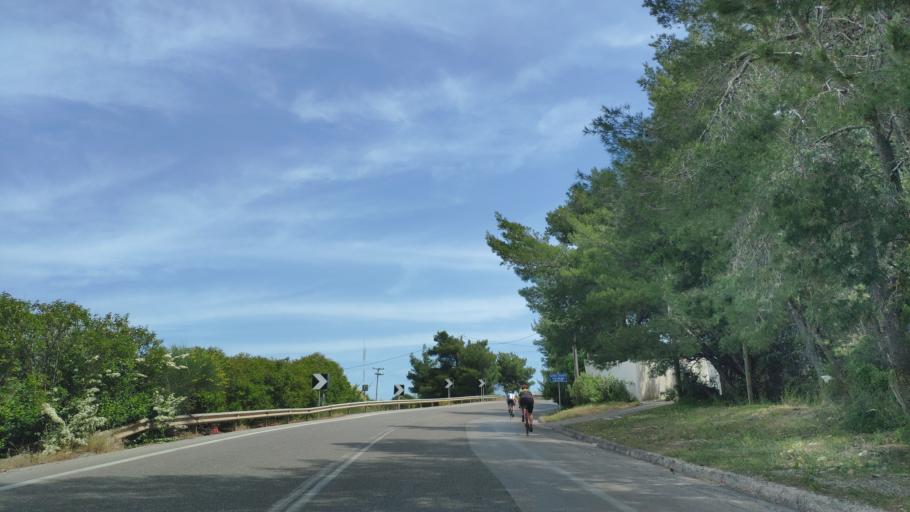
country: GR
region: Attica
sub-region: Nomarchia Anatolikis Attikis
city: Afidnes
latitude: 38.1981
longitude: 23.8533
